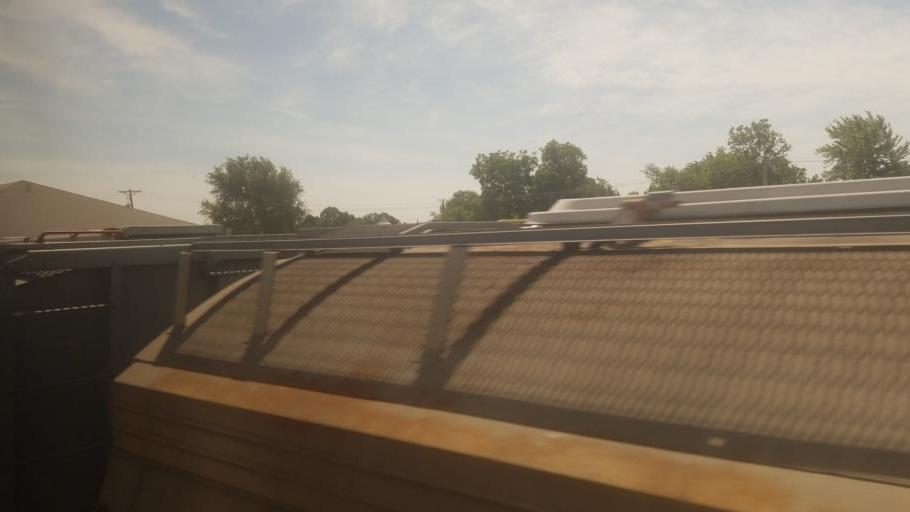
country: US
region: Missouri
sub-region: Carroll County
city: Carrollton
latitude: 39.3030
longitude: -93.6797
